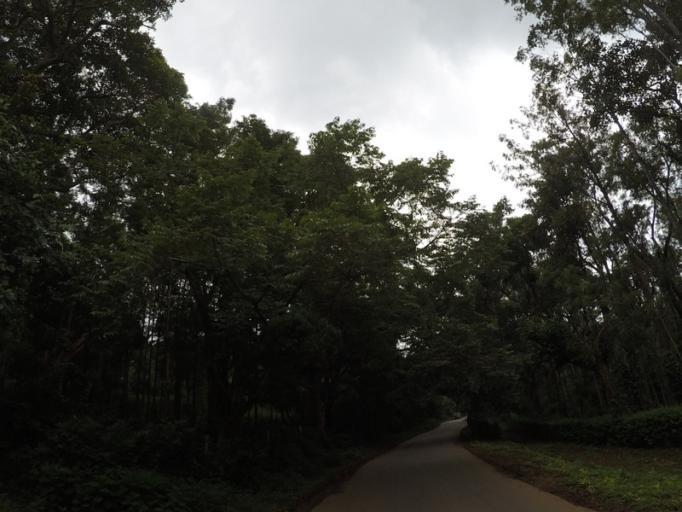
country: IN
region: Karnataka
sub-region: Chikmagalur
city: Chikmagalur
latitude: 13.4622
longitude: 75.7981
